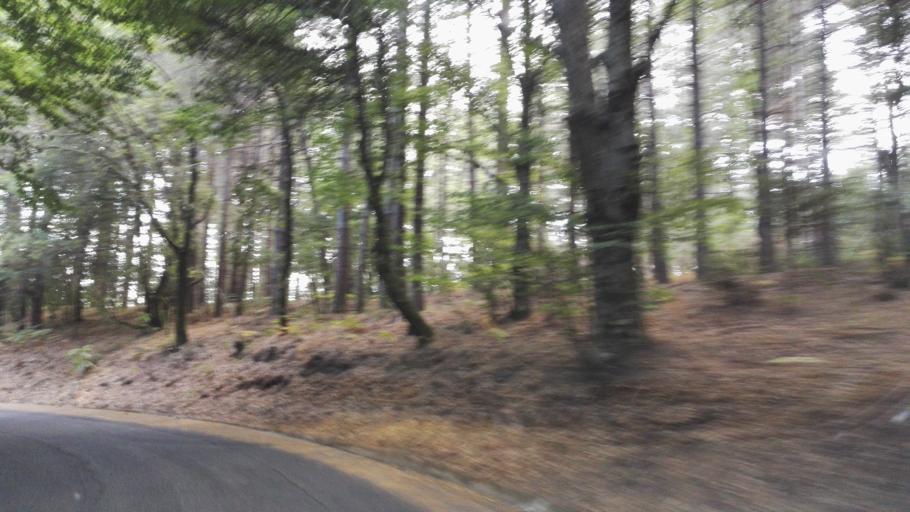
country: IT
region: Calabria
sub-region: Provincia di Vibo-Valentia
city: Nardodipace
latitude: 38.4820
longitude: 16.3427
